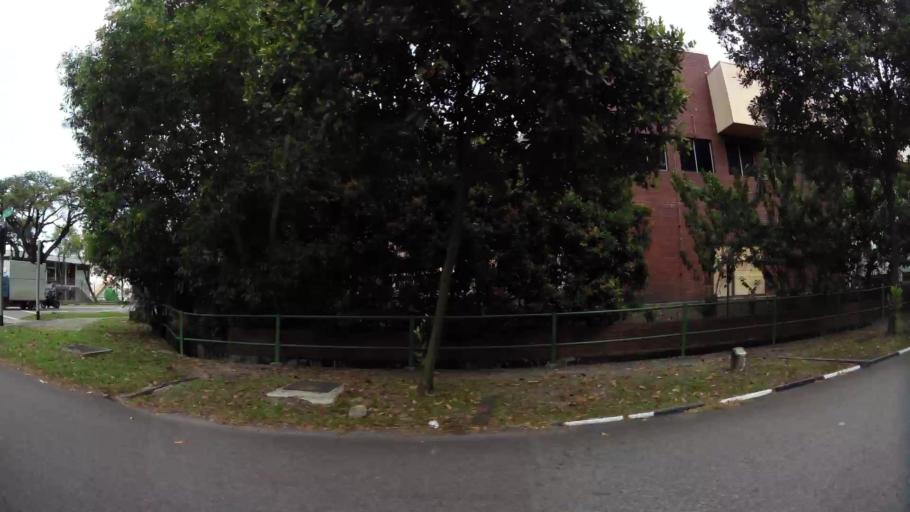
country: MY
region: Johor
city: Johor Bahru
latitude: 1.3170
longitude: 103.6614
